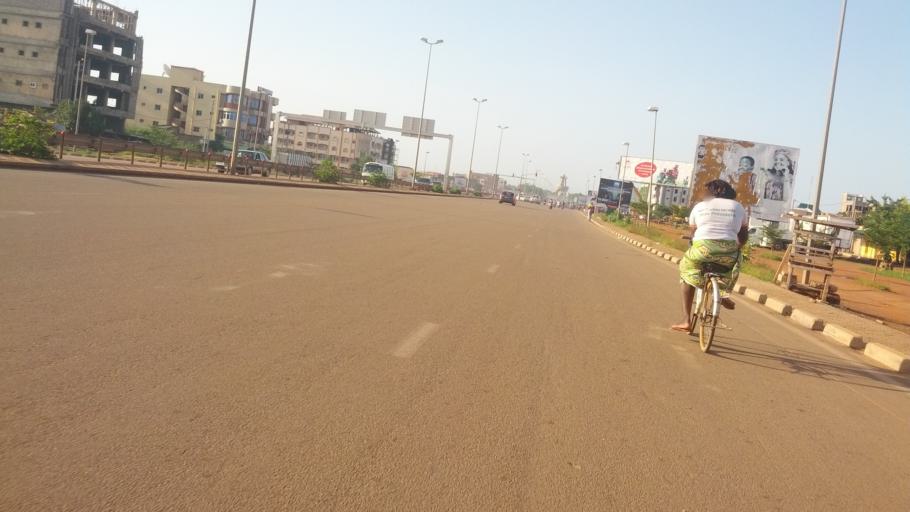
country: BF
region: Centre
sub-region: Kadiogo Province
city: Ouagadougou
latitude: 12.3296
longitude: -1.5027
